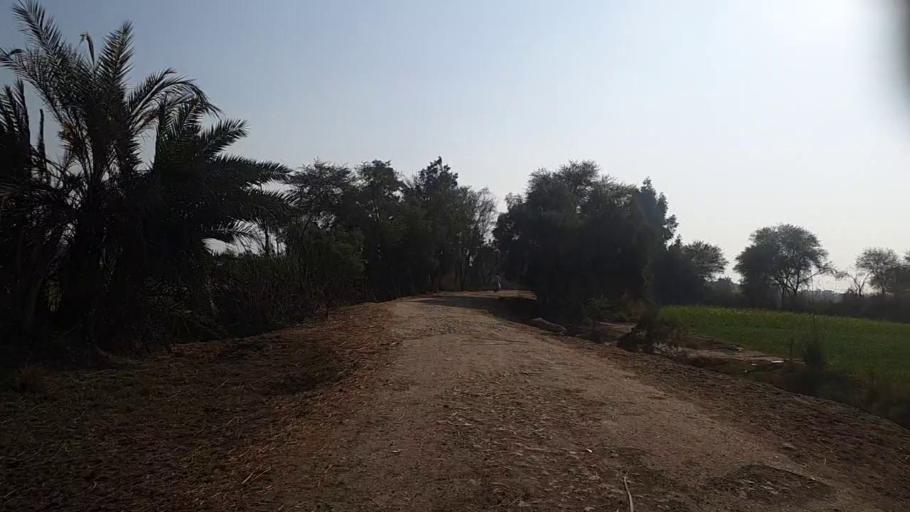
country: PK
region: Sindh
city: Mirpur Mathelo
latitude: 27.8937
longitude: 69.6077
